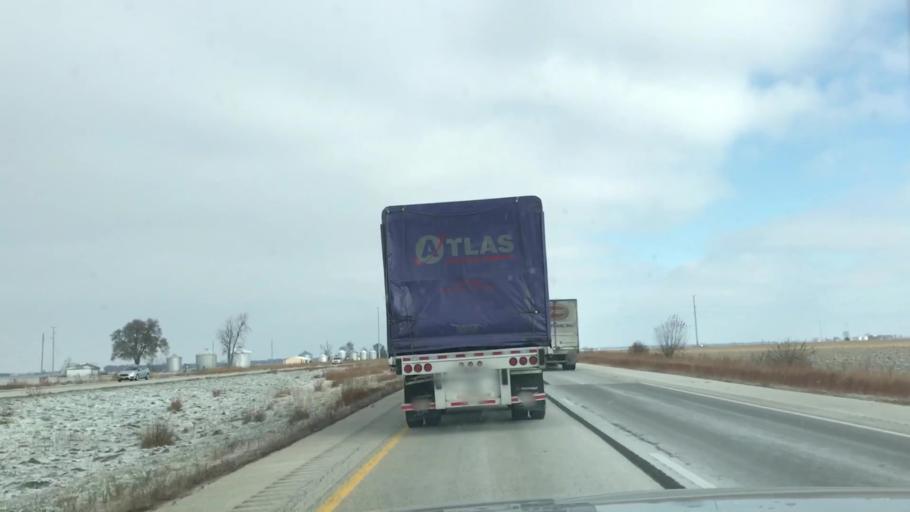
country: US
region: Illinois
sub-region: Sangamon County
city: Divernon
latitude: 39.5250
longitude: -89.6456
